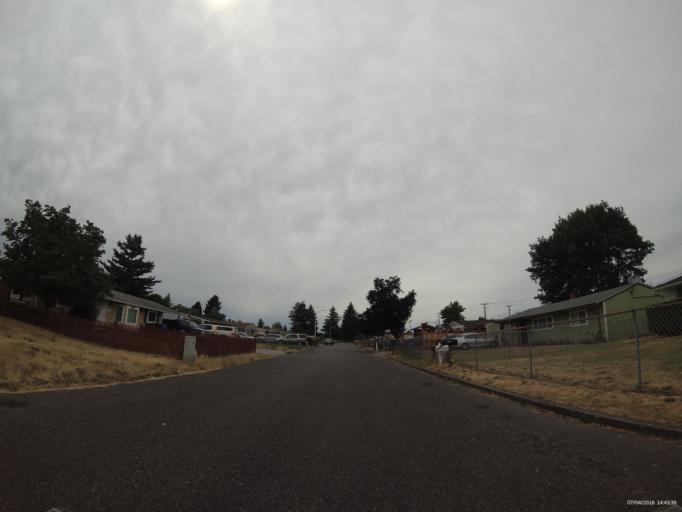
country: US
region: Washington
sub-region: Pierce County
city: Lakewood
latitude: 47.1661
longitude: -122.5018
